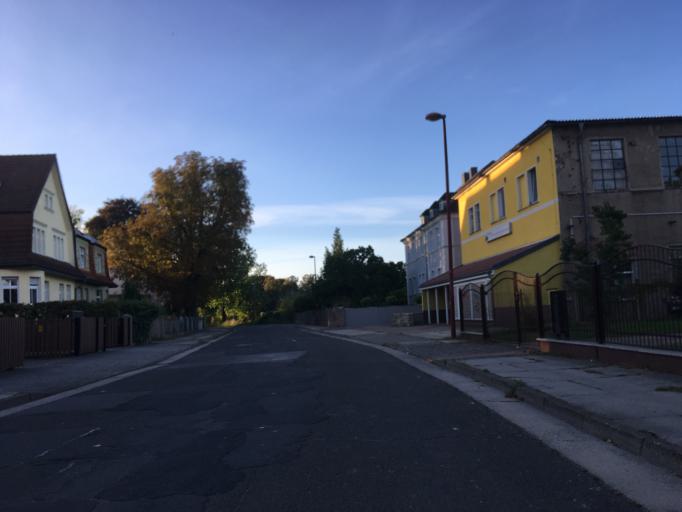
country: DE
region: Brandenburg
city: Forst
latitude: 51.7353
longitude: 14.6476
